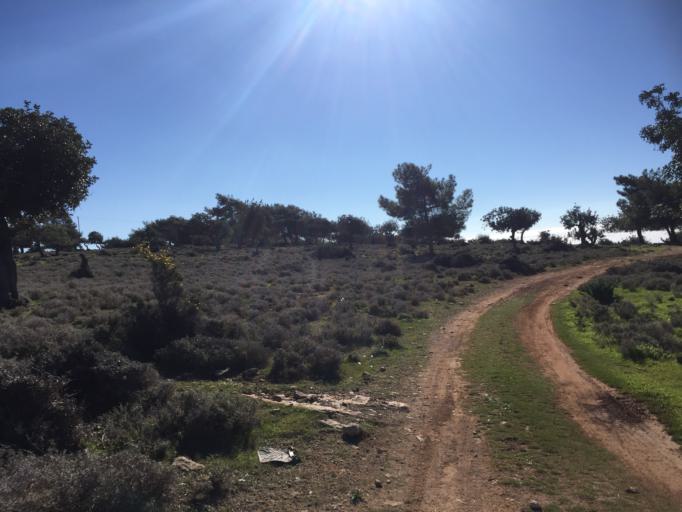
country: CY
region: Limassol
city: Pissouri
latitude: 34.6668
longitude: 32.6826
